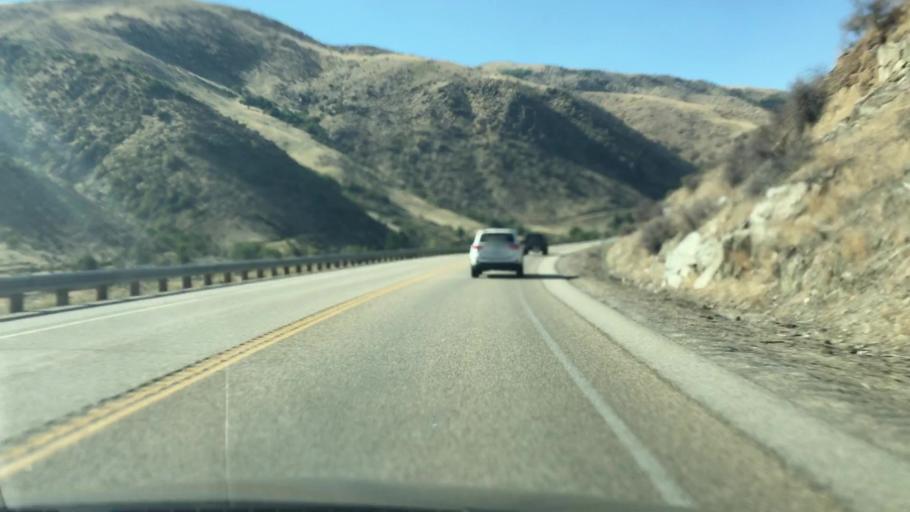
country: US
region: Idaho
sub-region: Ada County
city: Eagle
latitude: 43.9389
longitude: -116.1938
